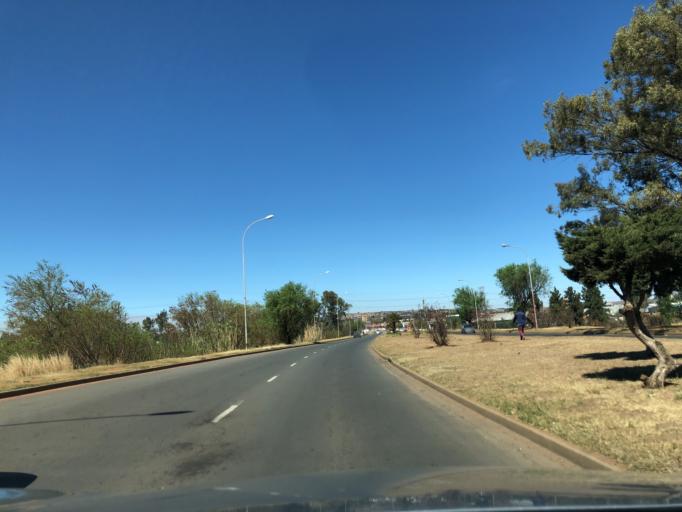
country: ZA
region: KwaZulu-Natal
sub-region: Amajuba District Municipality
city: Newcastle
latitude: -27.7448
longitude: 29.9374
